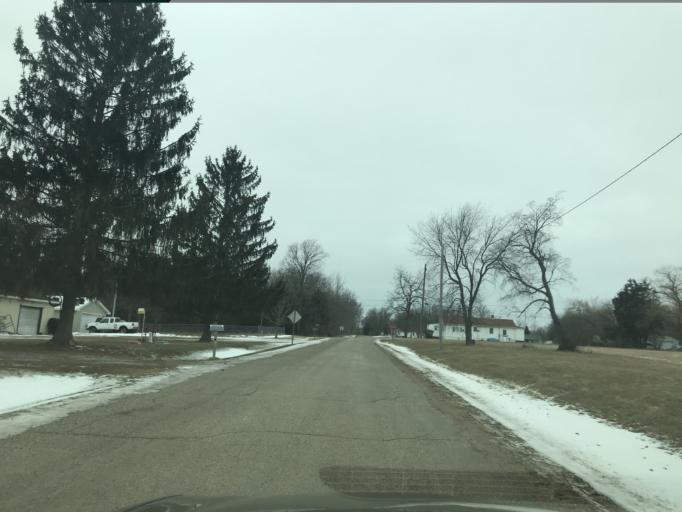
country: US
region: Michigan
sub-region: Jackson County
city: Brooklyn
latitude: 42.0660
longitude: -84.3330
